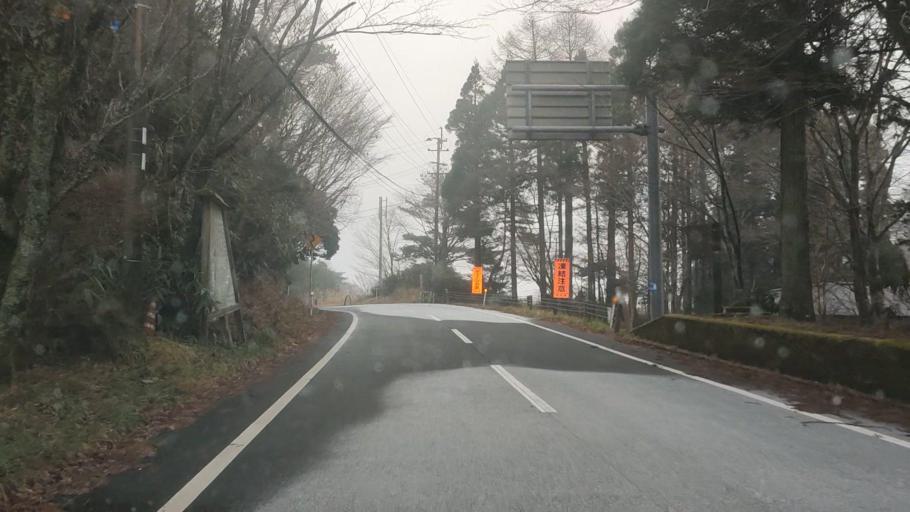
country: JP
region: Kumamoto
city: Matsubase
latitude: 32.5742
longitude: 130.9031
